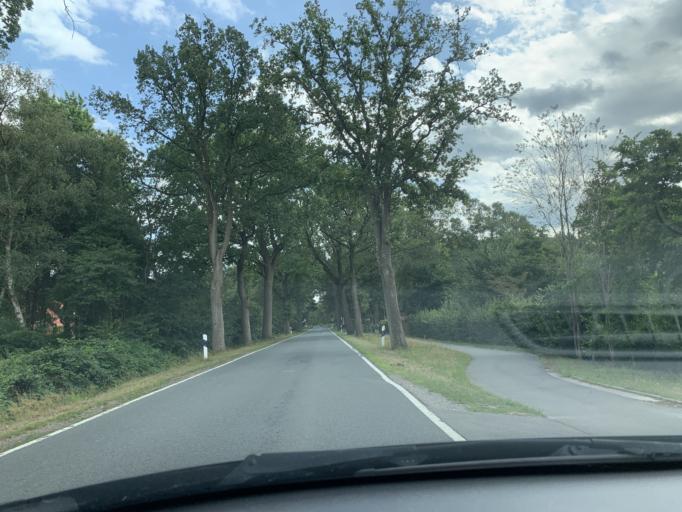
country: DE
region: Lower Saxony
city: Apen
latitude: 53.2588
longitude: 7.8452
